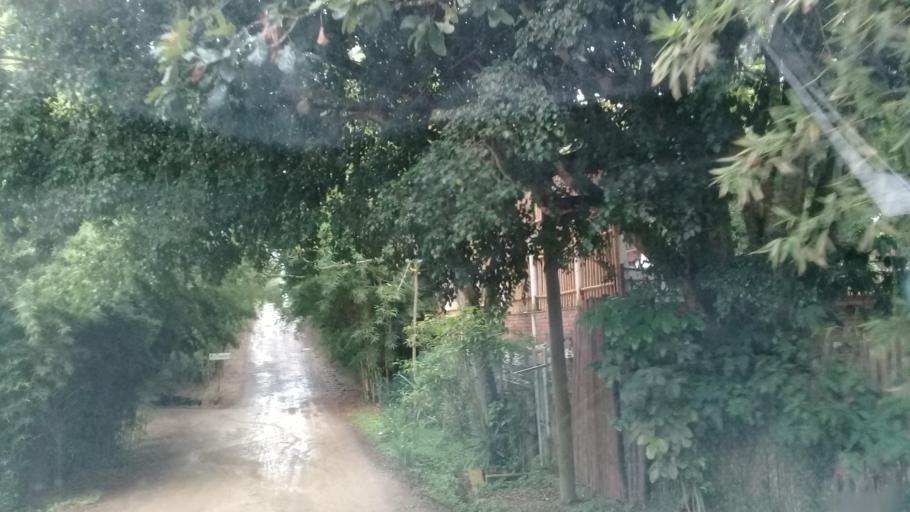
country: MX
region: Veracruz
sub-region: Emiliano Zapata
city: Jacarandas
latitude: 19.5056
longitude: -96.8442
